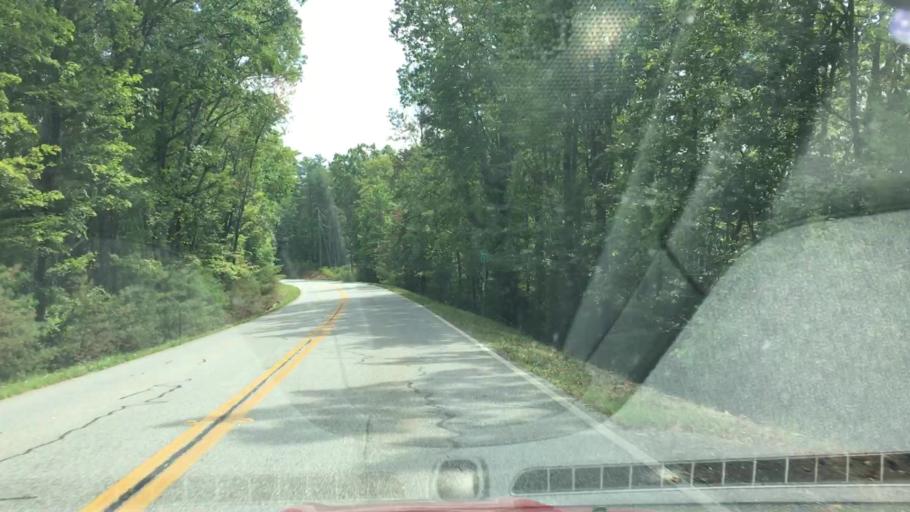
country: US
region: Georgia
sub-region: Murray County
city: Chatsworth
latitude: 34.7847
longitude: -84.6220
